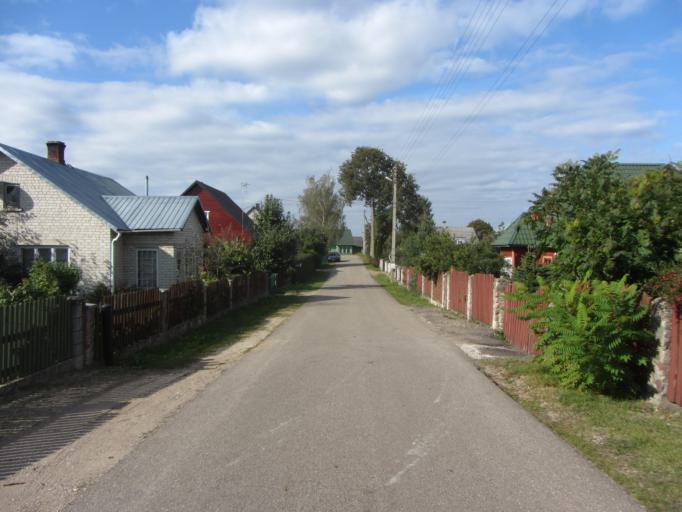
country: LT
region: Vilnius County
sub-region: Trakai
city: Rudiskes
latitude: 54.5178
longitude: 24.8260
